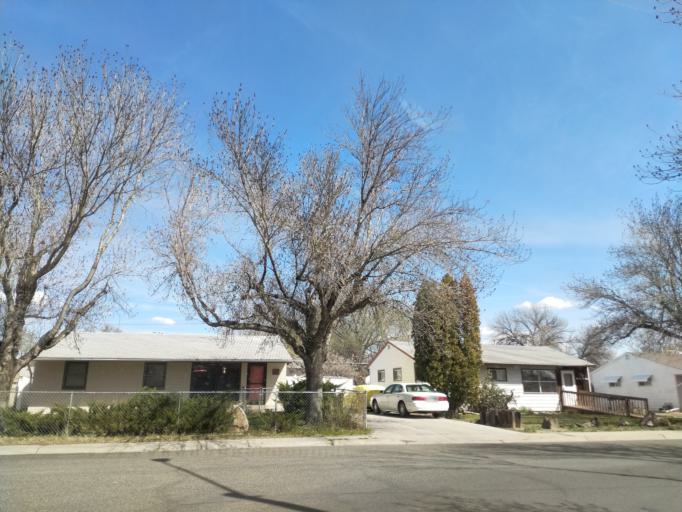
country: US
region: Colorado
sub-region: Mesa County
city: Grand Junction
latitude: 39.0800
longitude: -108.5407
